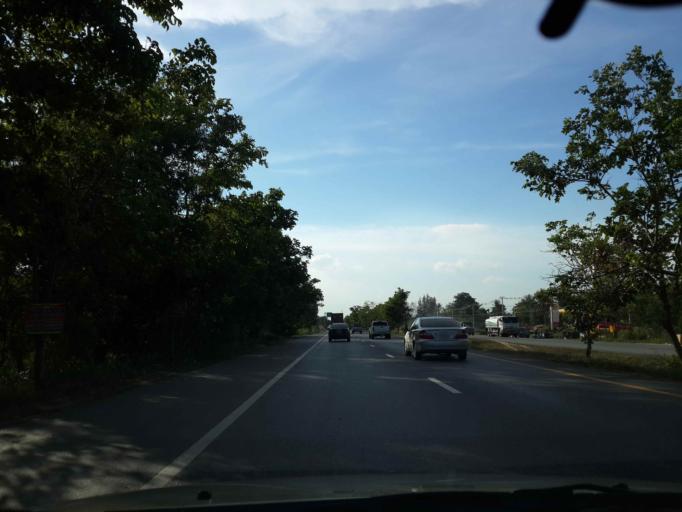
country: TH
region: Chon Buri
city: Phatthaya
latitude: 12.9420
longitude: 100.9944
